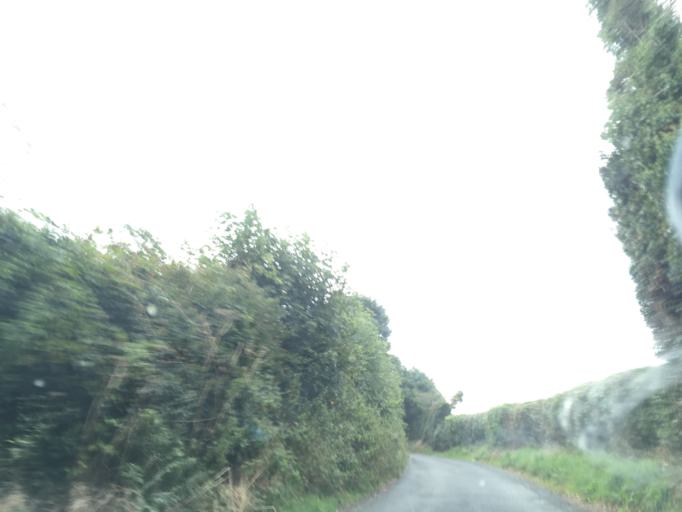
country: IE
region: Leinster
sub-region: Wicklow
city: Rathnew
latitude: 52.9231
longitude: -6.1047
